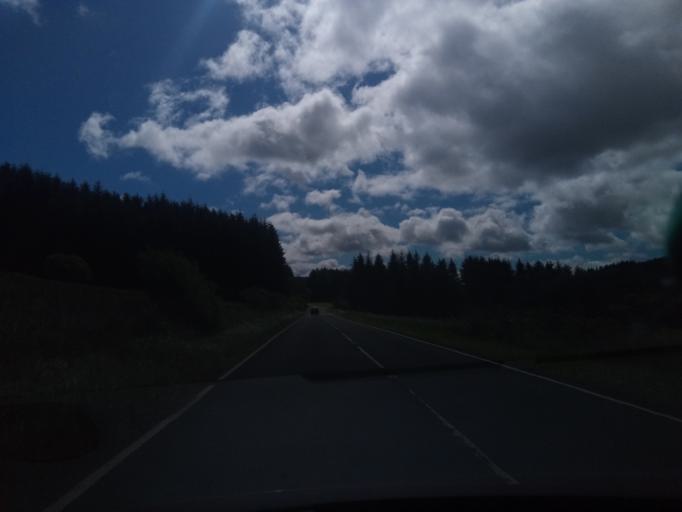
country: GB
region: England
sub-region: Northumberland
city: Rochester
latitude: 55.3203
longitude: -2.3769
